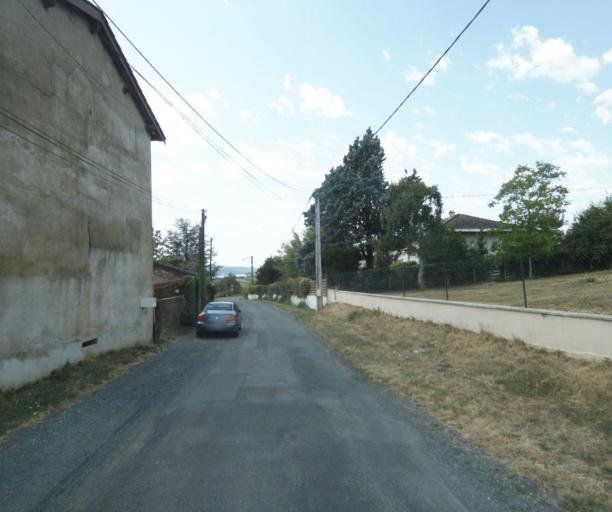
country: FR
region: Rhone-Alpes
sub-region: Departement du Rhone
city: Lentilly
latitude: 45.8350
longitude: 4.6571
